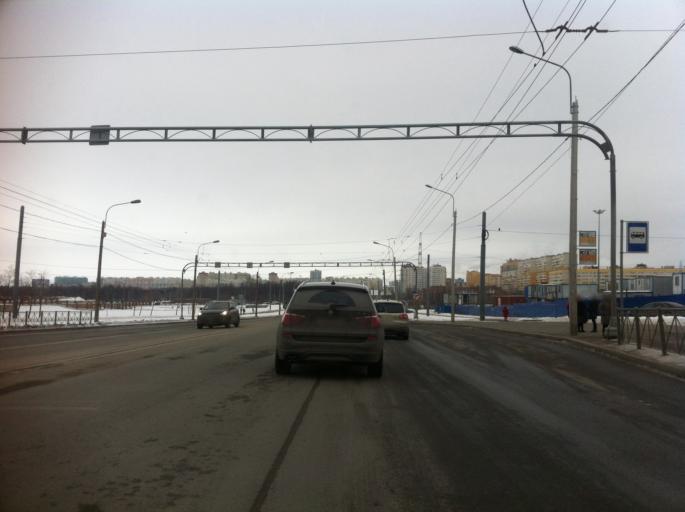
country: RU
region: St.-Petersburg
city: Uritsk
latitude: 59.8426
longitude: 30.1756
